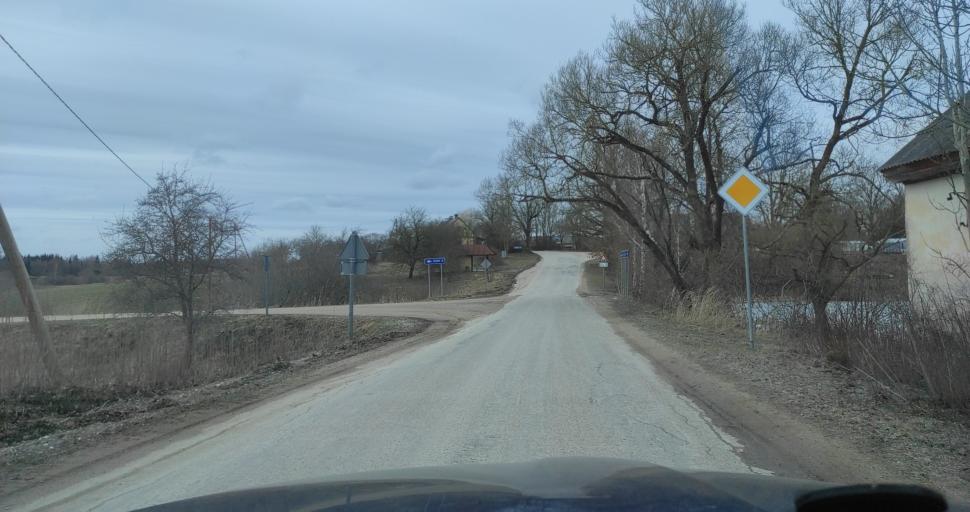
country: LV
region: Tukuma Rajons
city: Tukums
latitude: 57.0581
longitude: 23.0278
